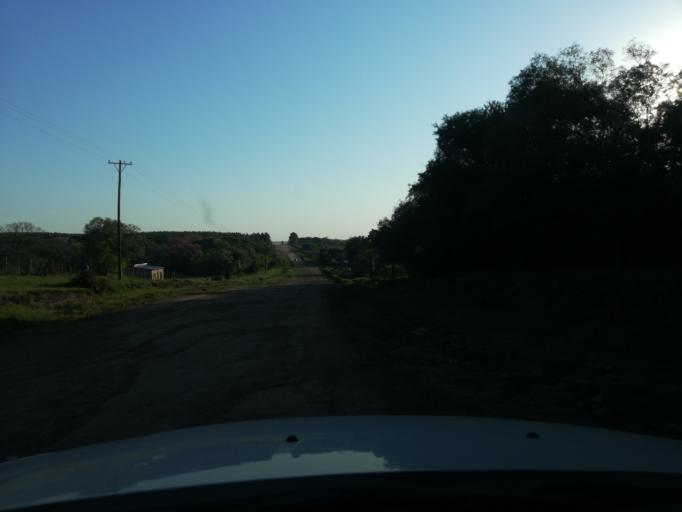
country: AR
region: Misiones
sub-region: Departamento de Apostoles
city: San Jose
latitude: -27.6327
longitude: -55.7327
